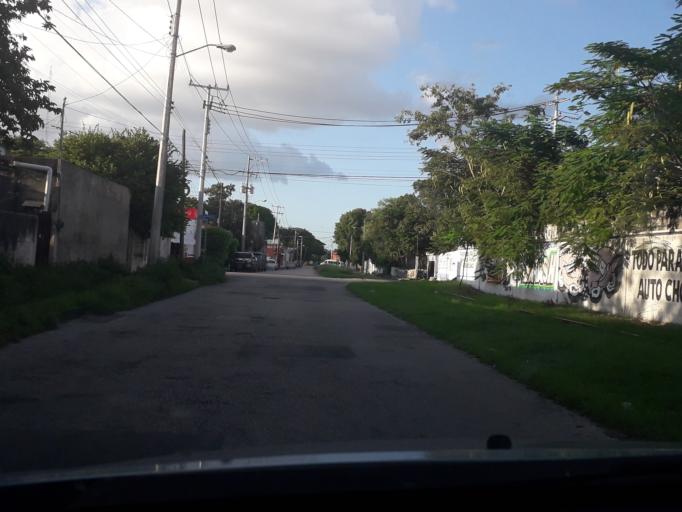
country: MX
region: Yucatan
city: Merida
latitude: 20.9642
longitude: -89.6438
